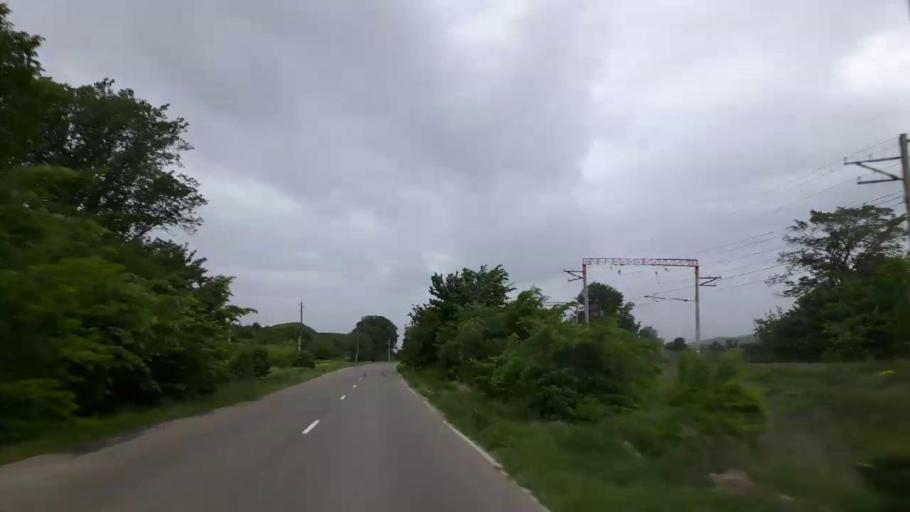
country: GE
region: Shida Kartli
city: Gori
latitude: 41.9942
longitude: 44.0281
